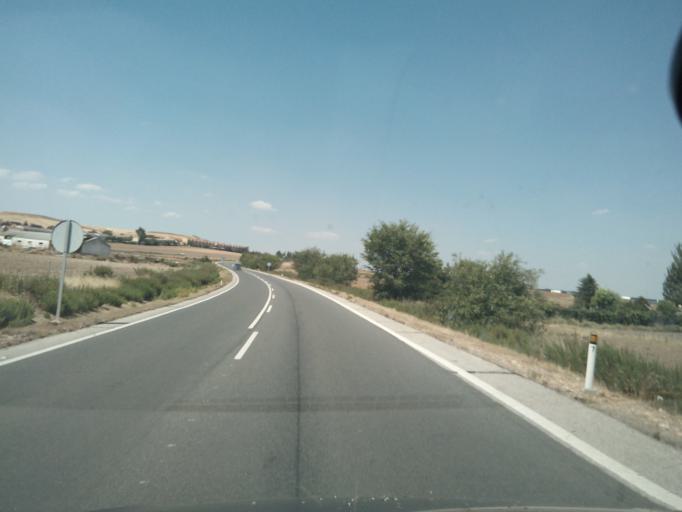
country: ES
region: Madrid
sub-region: Provincia de Madrid
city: Ajalvir
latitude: 40.5287
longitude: -3.4762
